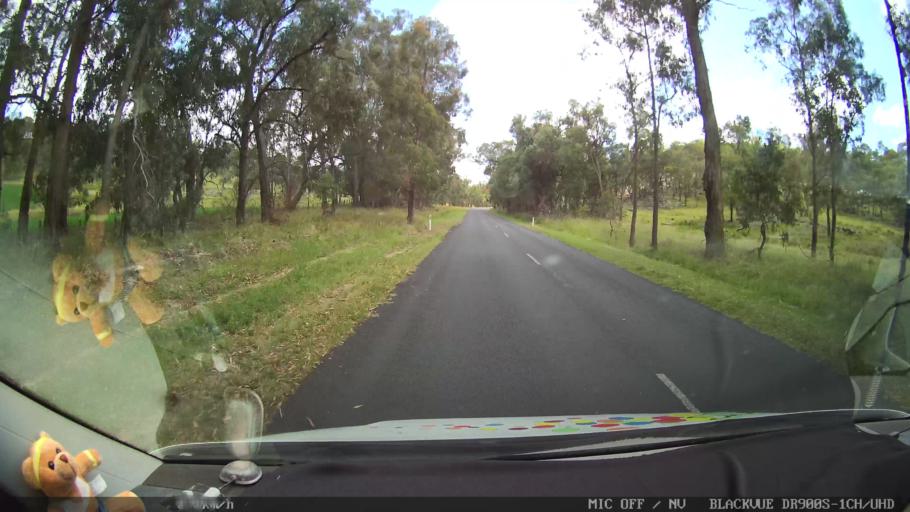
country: AU
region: New South Wales
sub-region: Glen Innes Severn
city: Glen Innes
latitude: -29.4920
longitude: 151.6823
